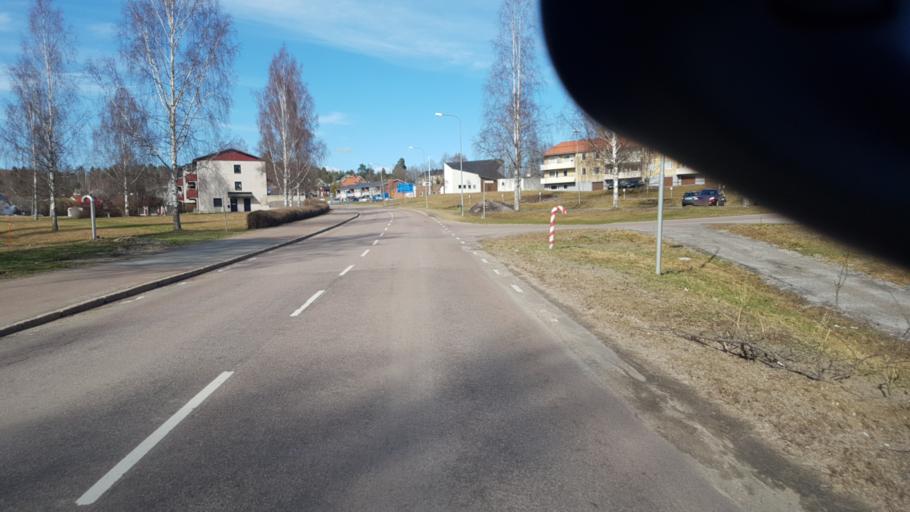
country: SE
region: Vaermland
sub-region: Eda Kommun
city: Amotfors
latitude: 59.7607
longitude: 12.3596
